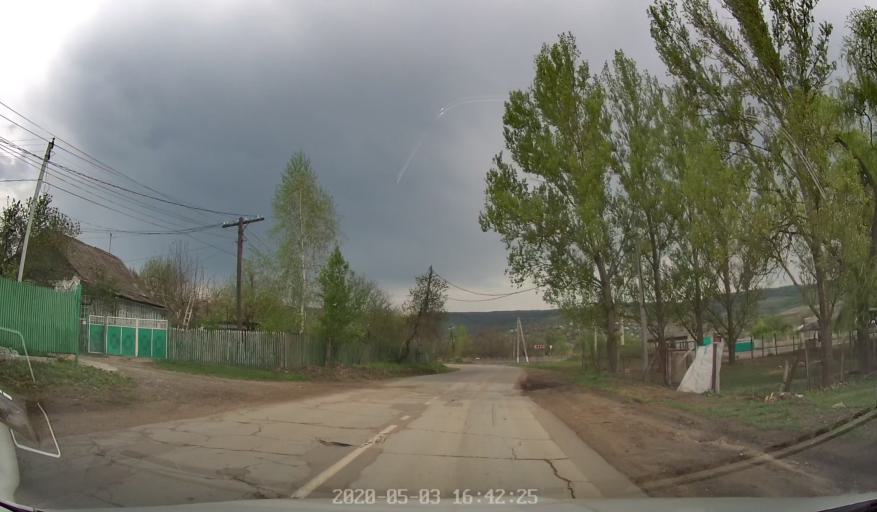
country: MD
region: Stinga Nistrului
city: Bucovat
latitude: 47.1600
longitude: 28.4202
